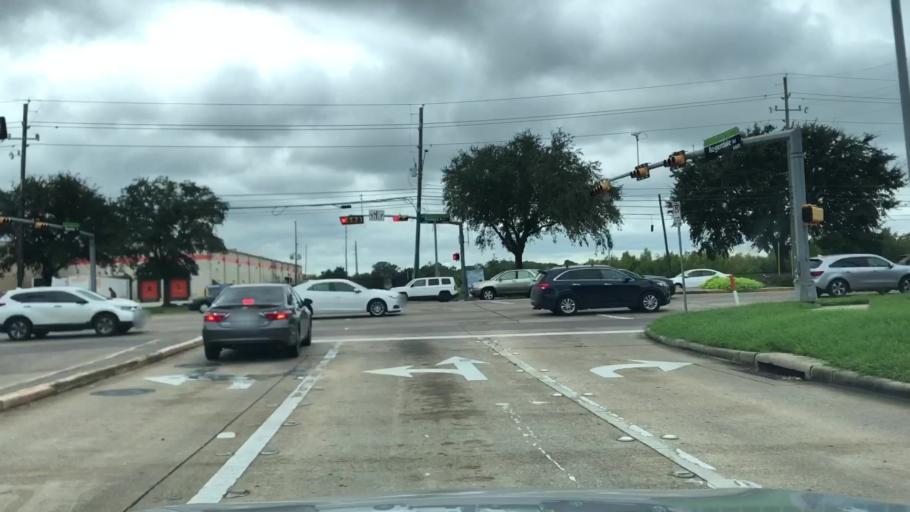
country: US
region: Texas
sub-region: Fort Bend County
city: Meadows Place
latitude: 29.7047
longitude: -95.5603
